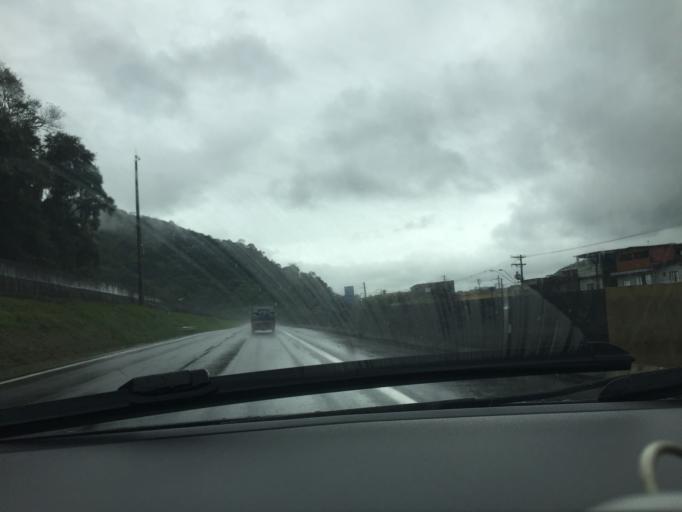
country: BR
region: Sao Paulo
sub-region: Cubatao
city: Cubatao
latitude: -23.8977
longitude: -46.4444
